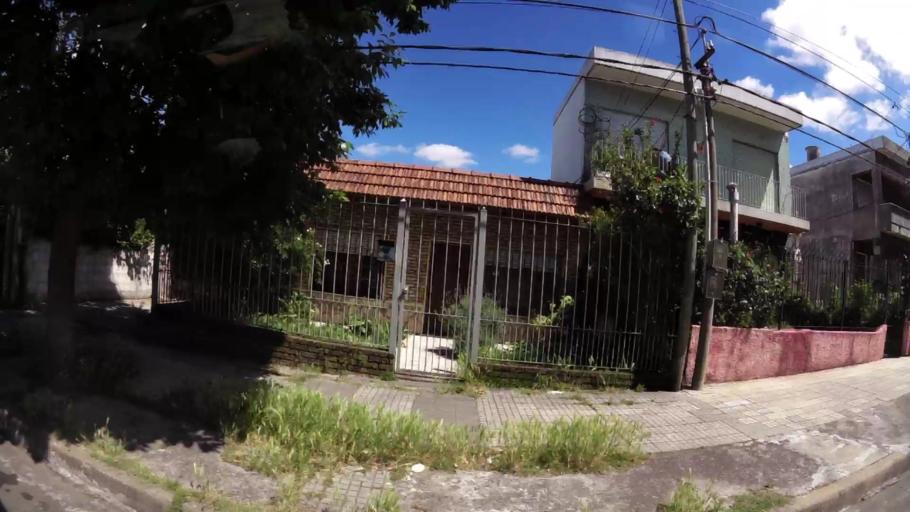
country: UY
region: Montevideo
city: Montevideo
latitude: -34.8584
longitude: -56.1387
